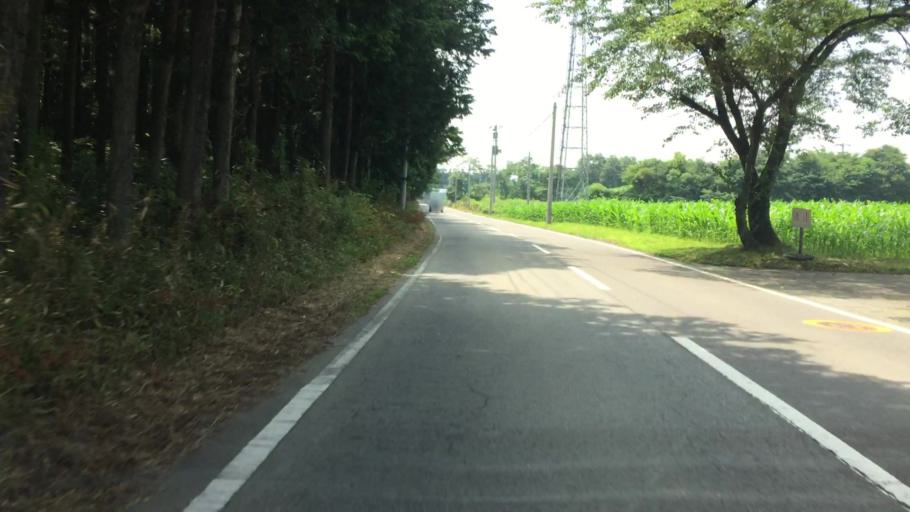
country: JP
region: Tochigi
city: Kuroiso
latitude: 36.9538
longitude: 139.9590
